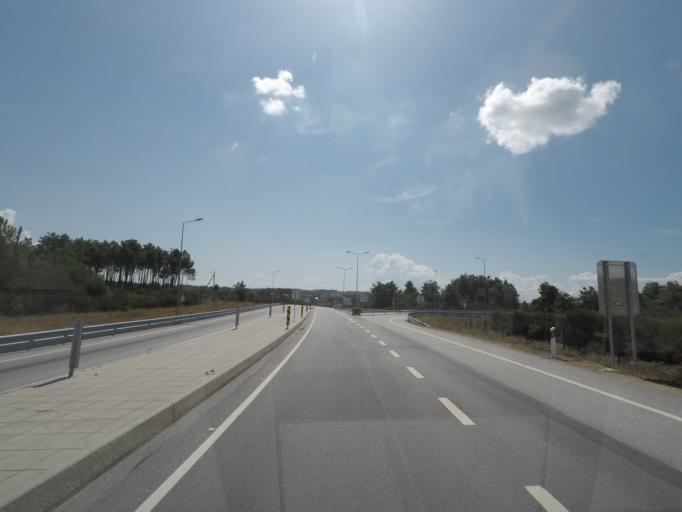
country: PT
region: Vila Real
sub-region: Murca
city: Murca
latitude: 41.3384
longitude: -7.4702
